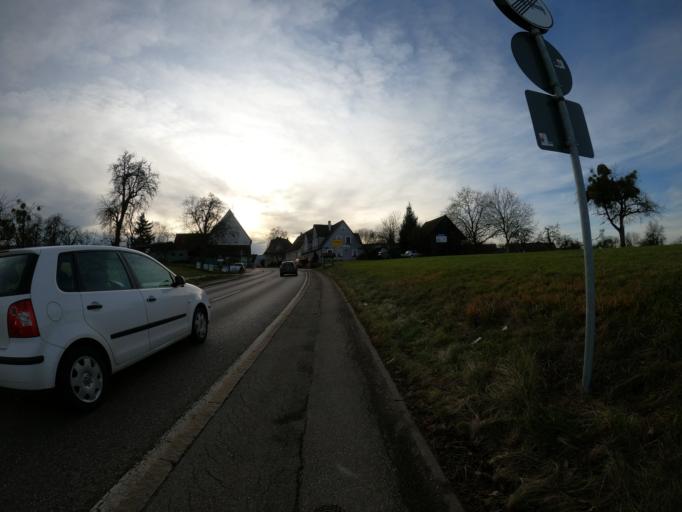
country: DE
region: Baden-Wuerttemberg
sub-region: Regierungsbezirk Stuttgart
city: Heiningen
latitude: 48.6671
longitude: 9.6476
